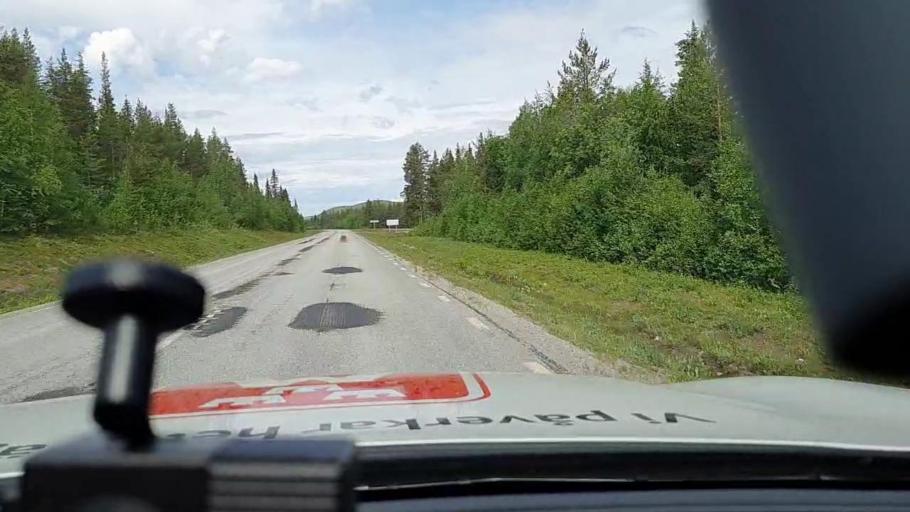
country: SE
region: Norrbotten
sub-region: Jokkmokks Kommun
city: Jokkmokk
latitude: 66.5518
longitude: 20.1181
